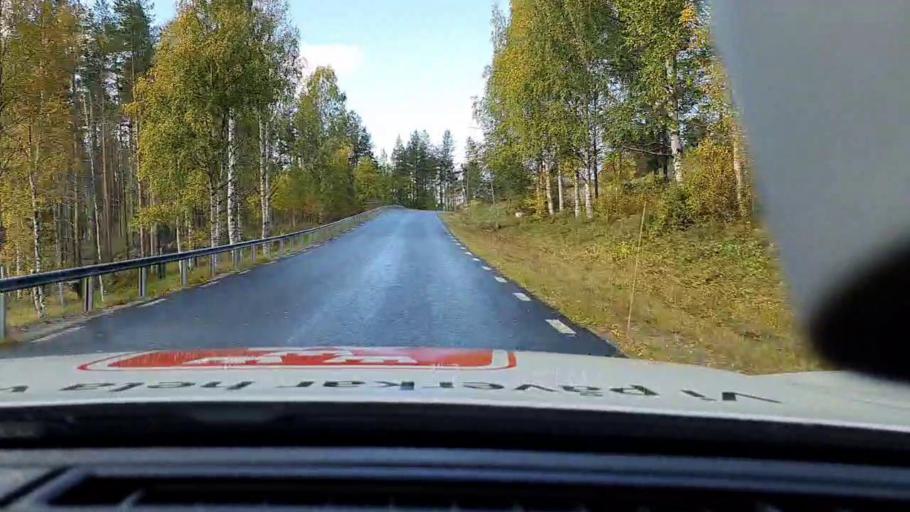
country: SE
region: Vaesterbotten
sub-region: Skelleftea Kommun
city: Langsele
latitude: 64.9460
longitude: 20.0262
